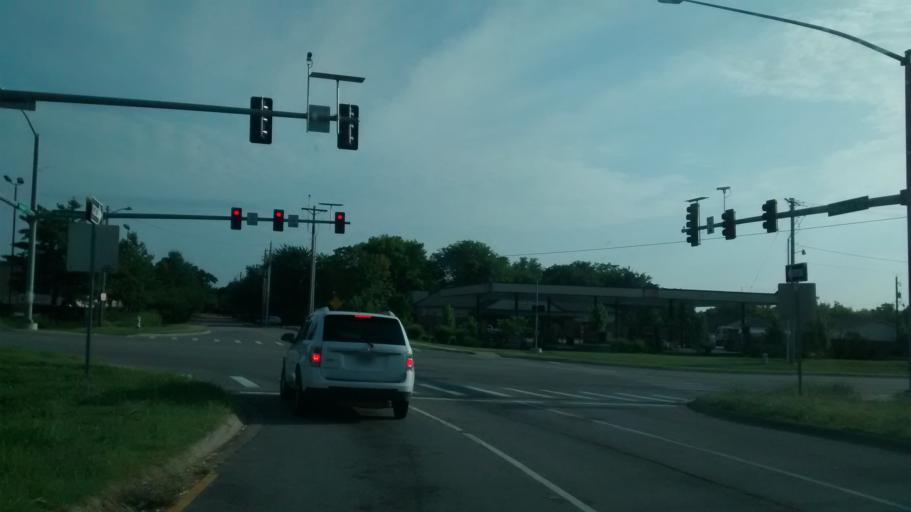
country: US
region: Arkansas
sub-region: Washington County
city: Fayetteville
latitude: 36.0779
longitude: -94.1985
